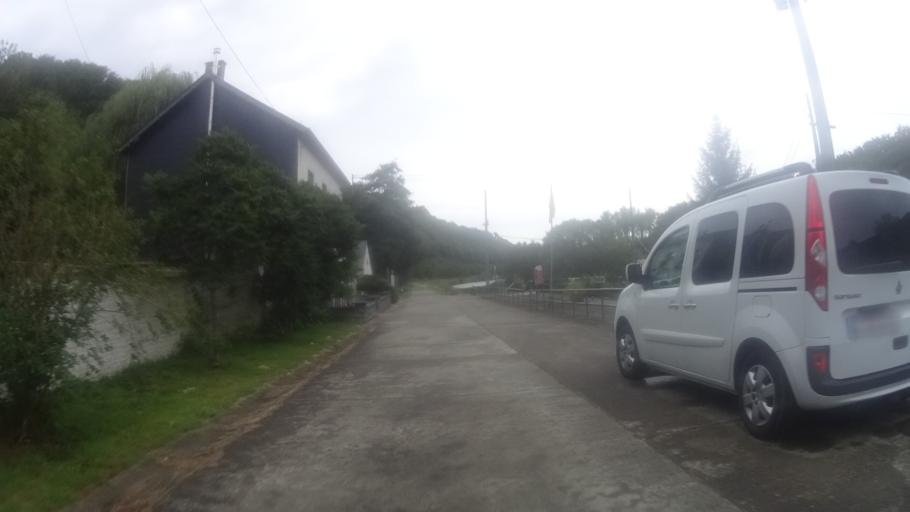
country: BE
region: Wallonia
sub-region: Province du Hainaut
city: Thuin
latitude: 50.3495
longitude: 4.3084
